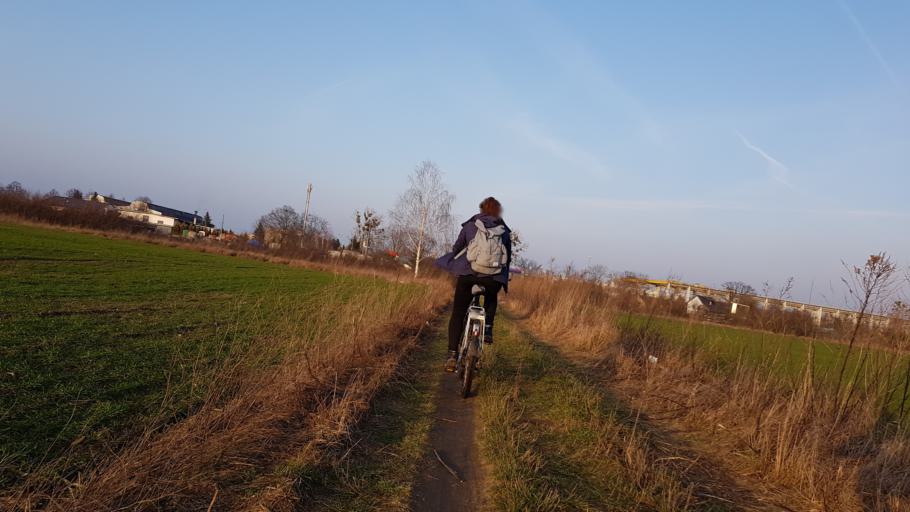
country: PL
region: West Pomeranian Voivodeship
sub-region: Powiat mysliborski
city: Barlinek
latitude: 52.9900
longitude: 15.1924
